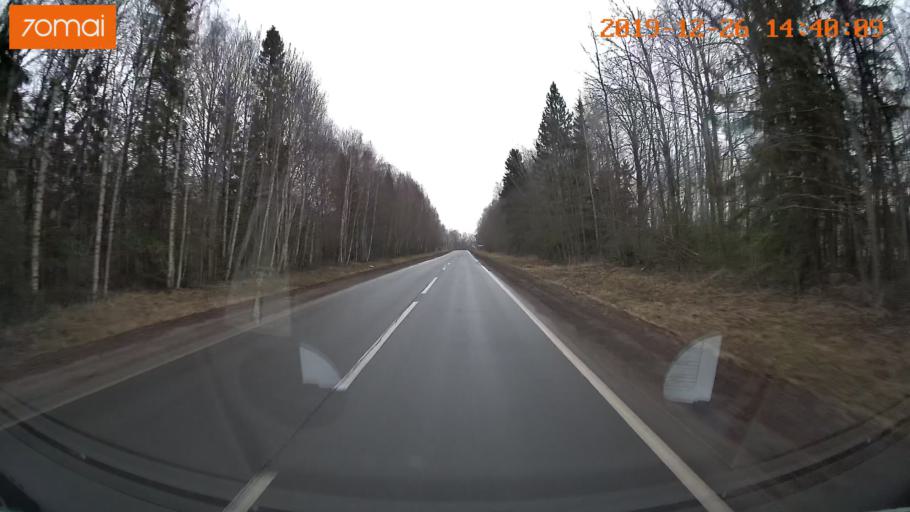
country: RU
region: Jaroslavl
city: Poshekhon'ye
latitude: 58.3777
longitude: 38.9930
